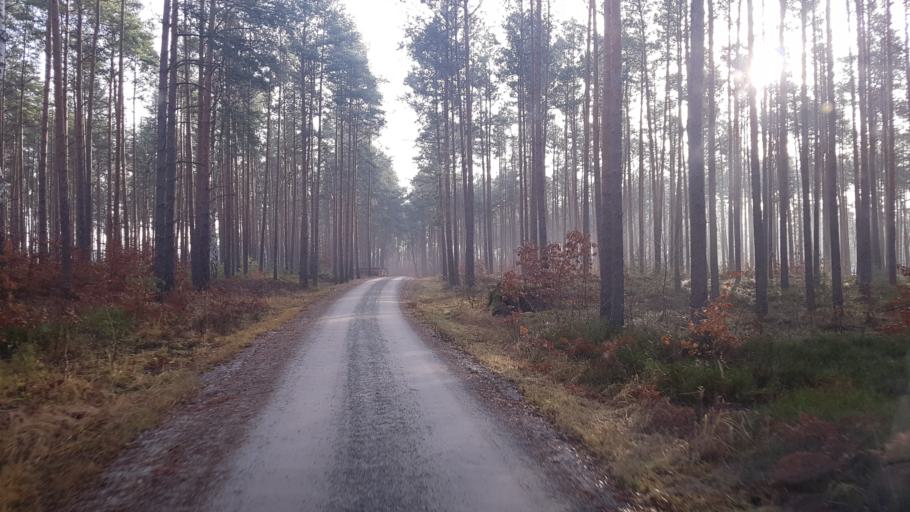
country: DE
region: Brandenburg
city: Schonborn
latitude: 51.6205
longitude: 13.5105
